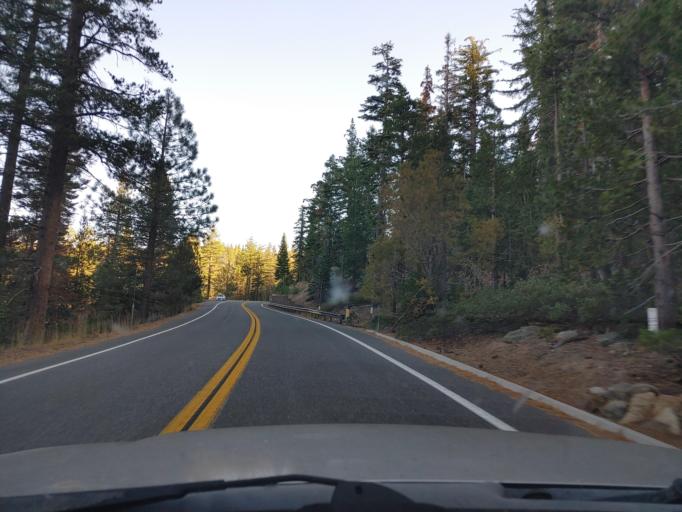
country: US
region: California
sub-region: Placer County
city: Tahoma
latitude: 38.9893
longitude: -120.1101
